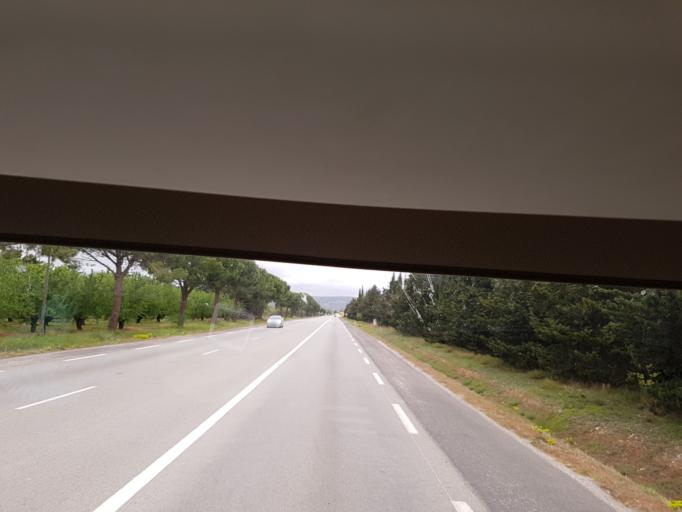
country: FR
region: Languedoc-Roussillon
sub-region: Departement des Pyrenees-Orientales
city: Salses-le-Chateau
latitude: 42.8168
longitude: 2.9149
